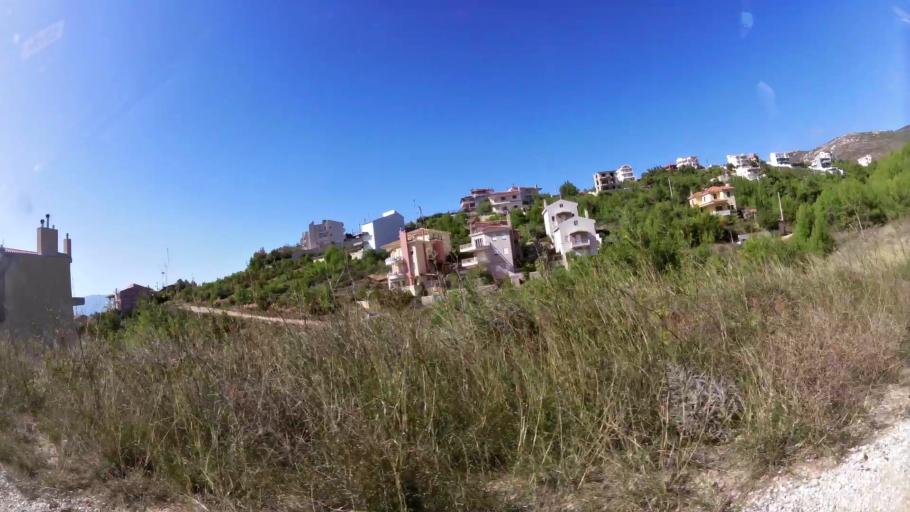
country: GR
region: Attica
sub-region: Nomarchia Anatolikis Attikis
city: Dioni
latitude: 38.0335
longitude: 23.9348
